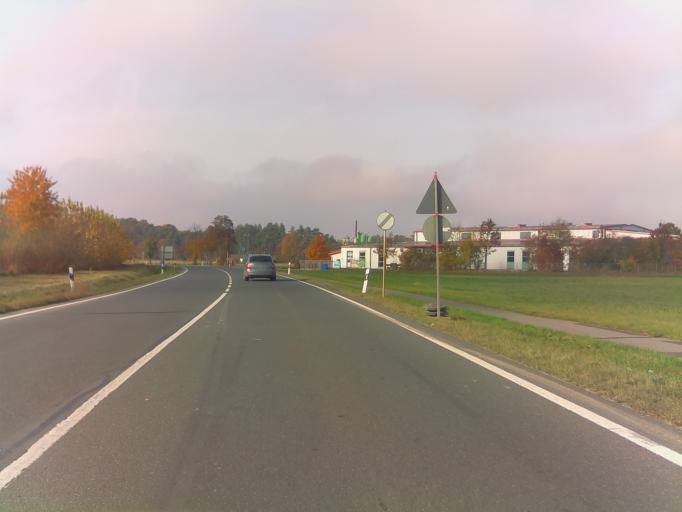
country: DE
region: Bavaria
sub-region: Regierungsbezirk Unterfranken
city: Sommerach
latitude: 49.8016
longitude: 10.2123
